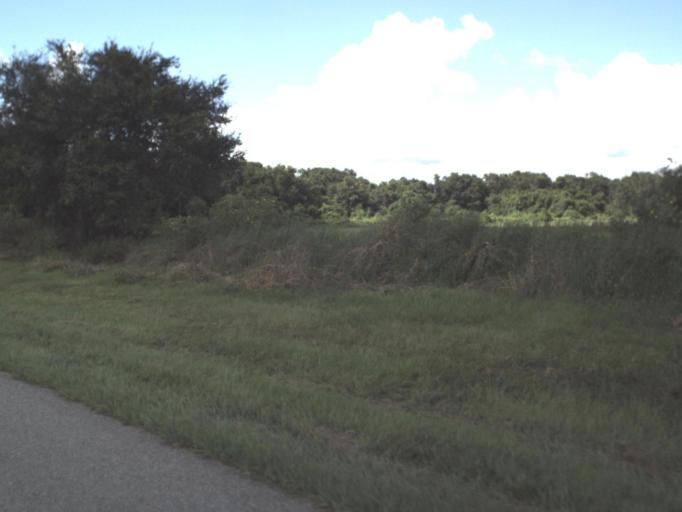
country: US
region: Florida
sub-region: Sarasota County
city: Lake Sarasota
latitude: 27.3656
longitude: -82.2071
